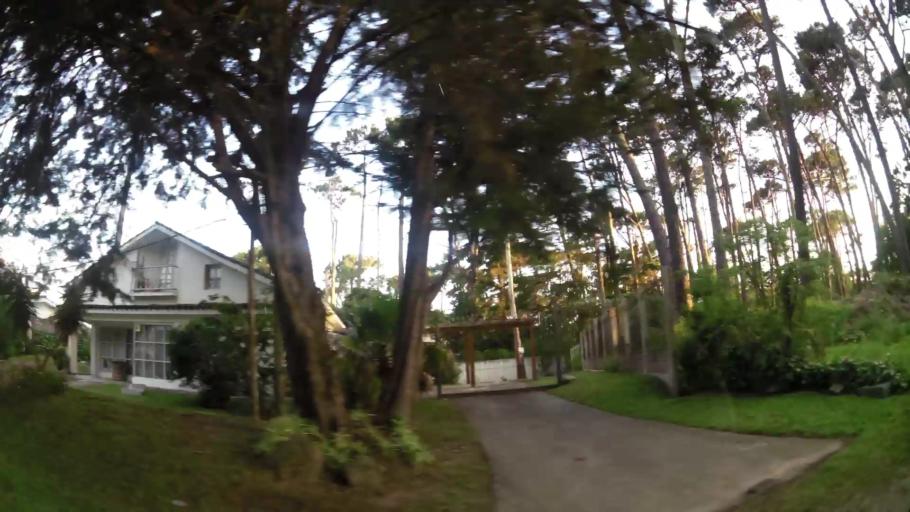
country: UY
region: Maldonado
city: Maldonado
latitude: -34.9313
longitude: -54.9363
